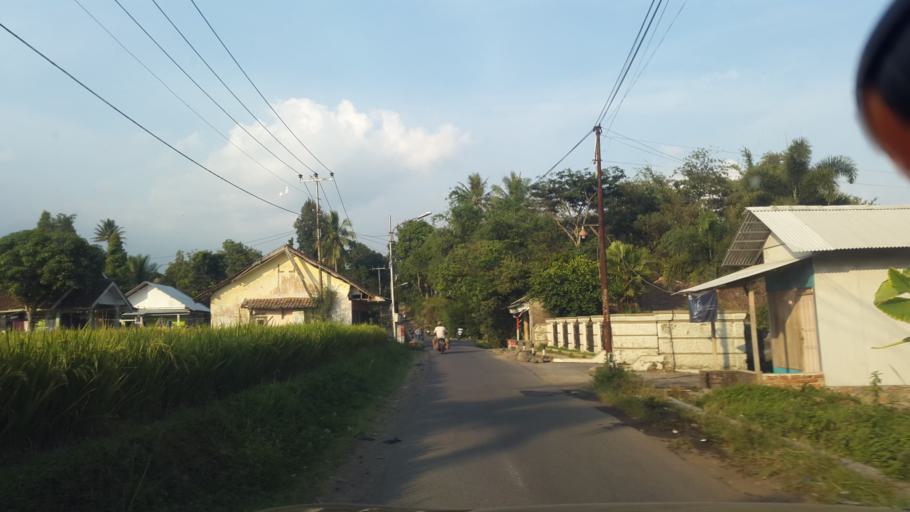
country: ID
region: West Java
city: Sukabumi
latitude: -6.8729
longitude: 106.8706
